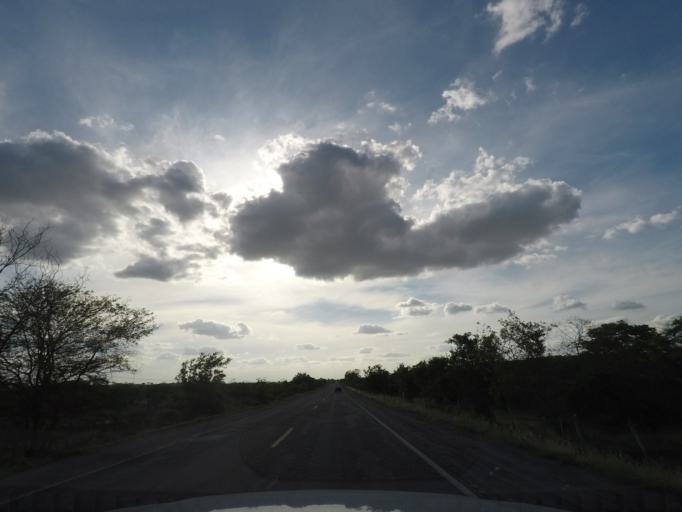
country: BR
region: Bahia
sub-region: Anguera
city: Anguera
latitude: -12.1850
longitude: -39.4773
